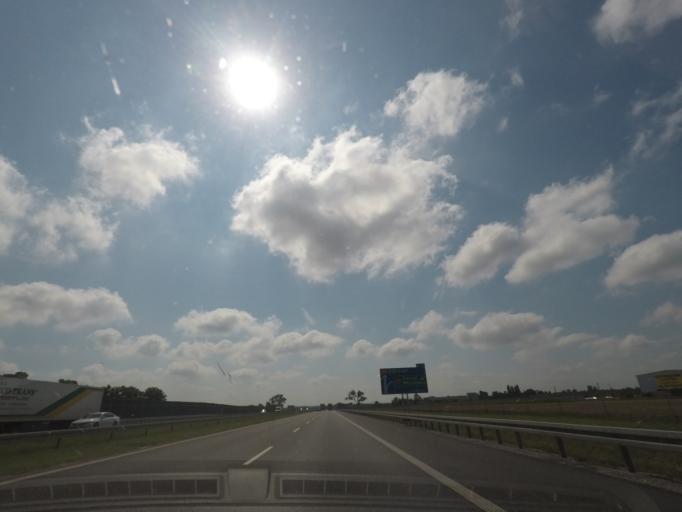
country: PL
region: Kujawsko-Pomorskie
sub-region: Powiat wloclawski
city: Brzesc Kujawski
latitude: 52.6339
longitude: 18.9547
